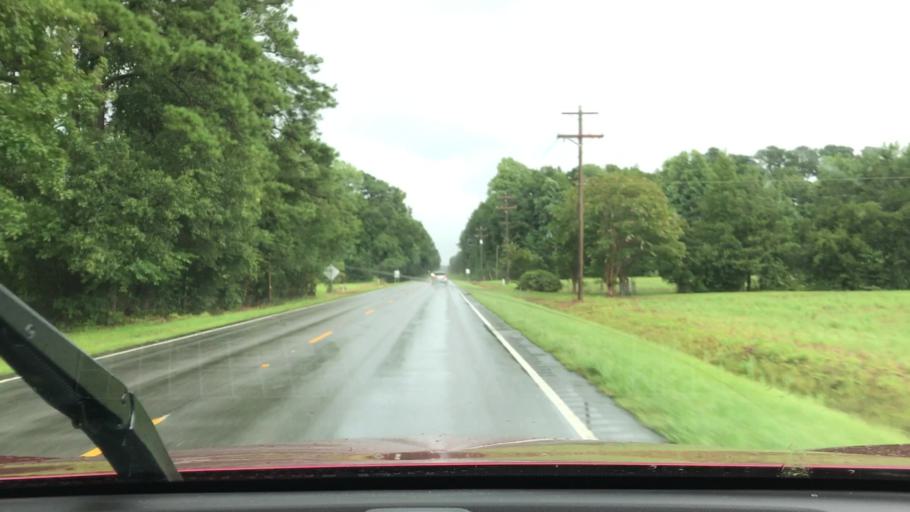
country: US
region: South Carolina
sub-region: Horry County
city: Socastee
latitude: 33.7032
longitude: -79.1059
